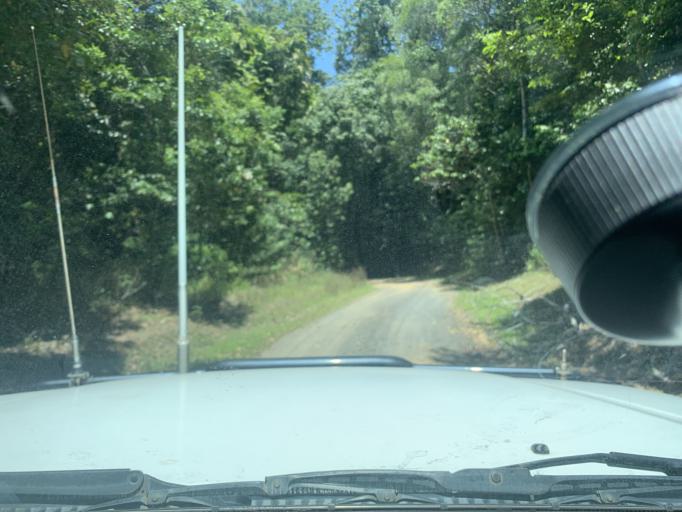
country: AU
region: Queensland
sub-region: Cairns
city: Redlynch
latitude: -16.9648
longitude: 145.6460
